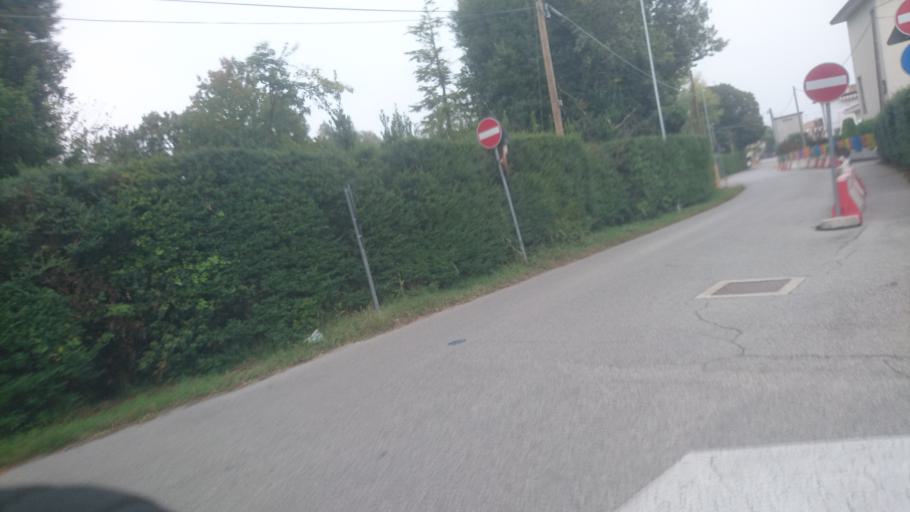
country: IT
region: Veneto
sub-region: Provincia di Padova
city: Selvazzano Dentro
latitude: 45.3958
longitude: 11.7795
